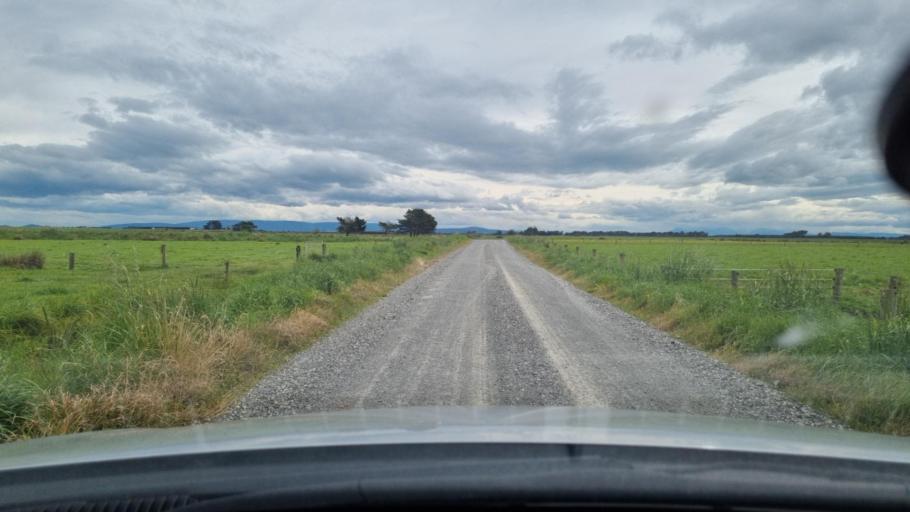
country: NZ
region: Southland
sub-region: Invercargill City
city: Invercargill
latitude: -46.4020
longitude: 168.2849
